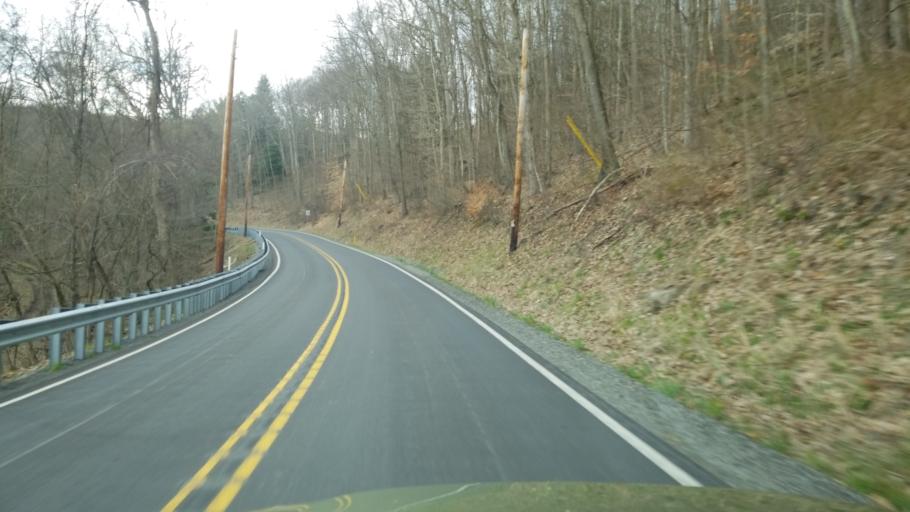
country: US
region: Pennsylvania
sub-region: Clearfield County
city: Curwensville
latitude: 40.8541
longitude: -78.4470
